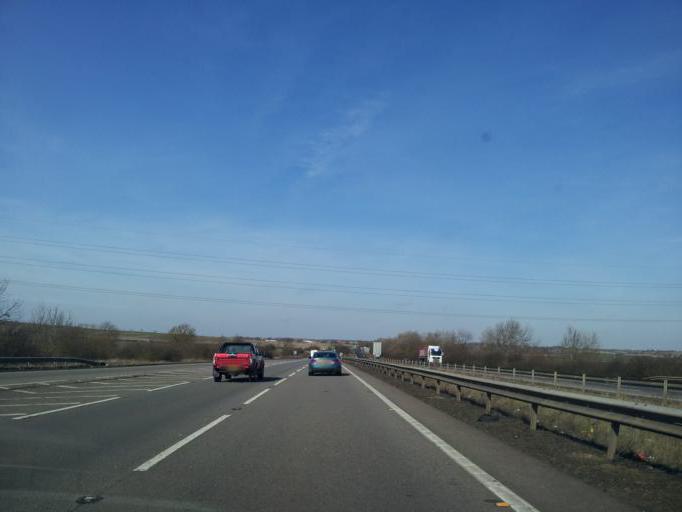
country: GB
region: England
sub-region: Cambridgeshire
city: Brampton
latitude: 52.3356
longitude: -0.2498
